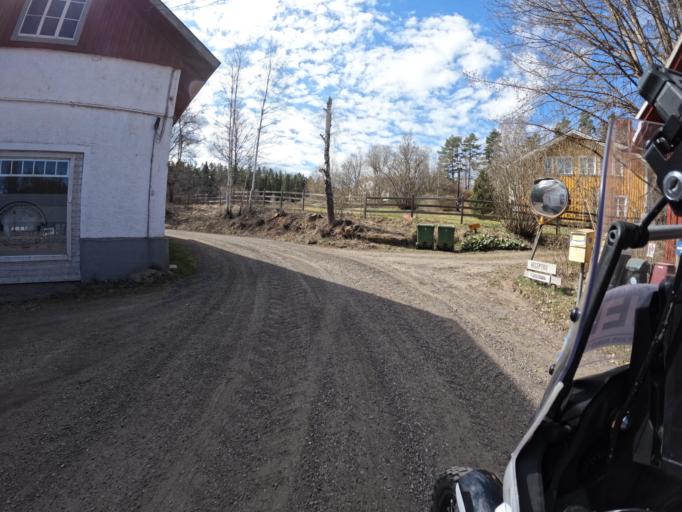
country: SE
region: Joenkoeping
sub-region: Mullsjo Kommun
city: Mullsjoe
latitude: 57.9952
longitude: 13.8457
